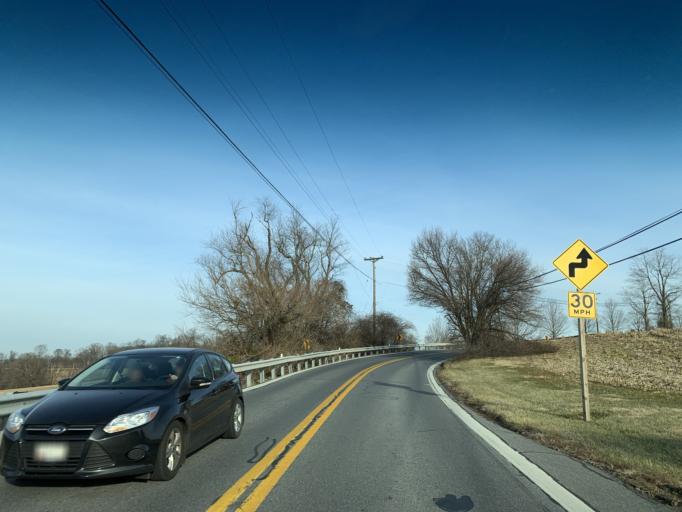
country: US
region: Maryland
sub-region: Carroll County
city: Hampstead
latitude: 39.6018
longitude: -76.7847
